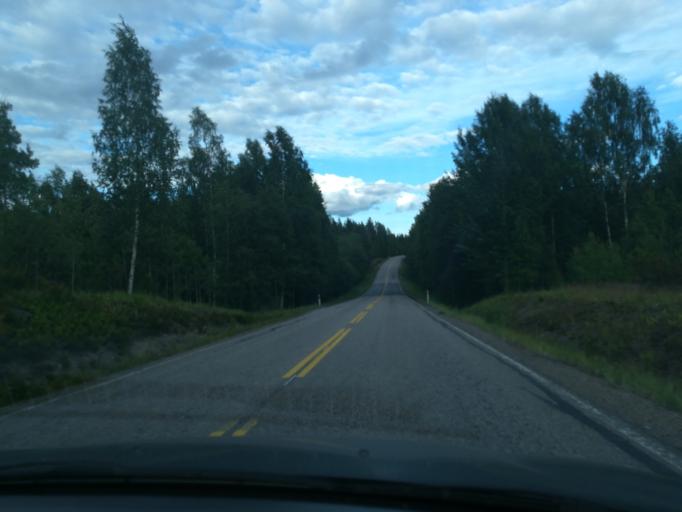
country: FI
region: Southern Savonia
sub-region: Mikkeli
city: Puumala
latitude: 61.5643
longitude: 28.0955
